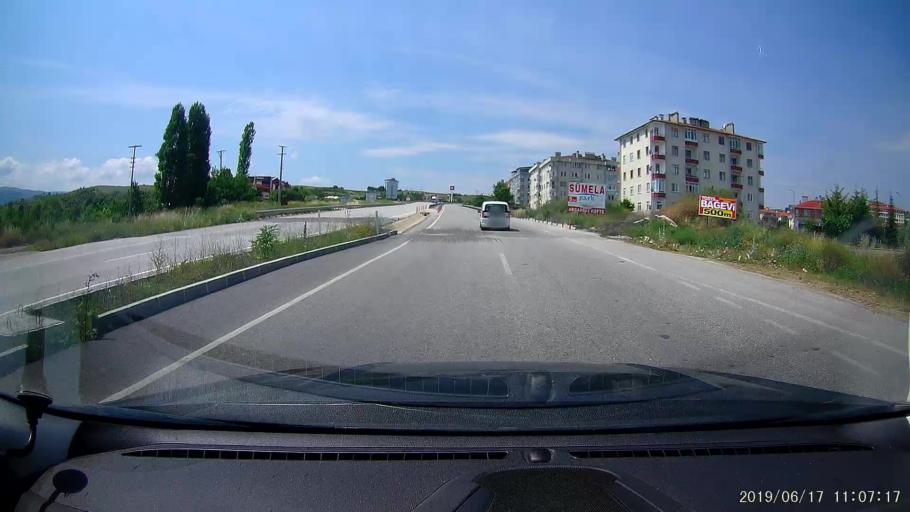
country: TR
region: Kastamonu
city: Tosya
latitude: 41.0048
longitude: 34.0561
